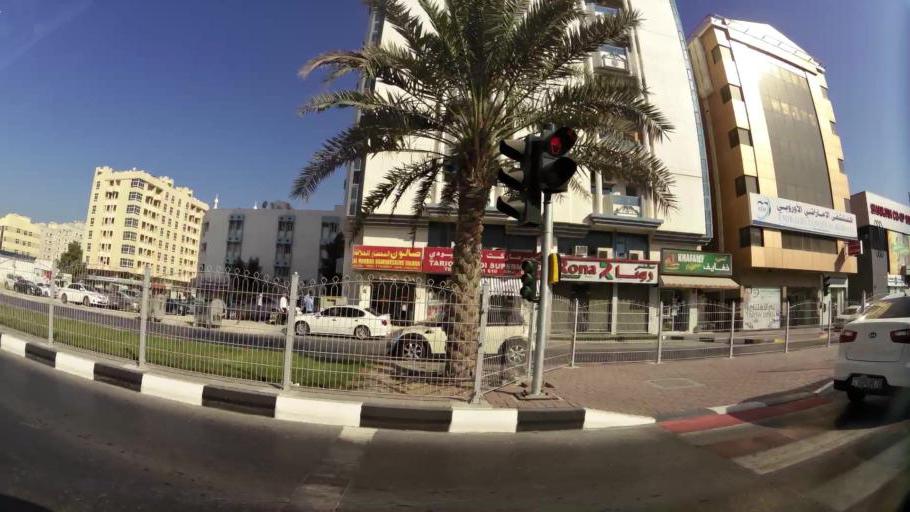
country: AE
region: Ash Shariqah
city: Sharjah
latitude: 25.3731
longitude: 55.3995
